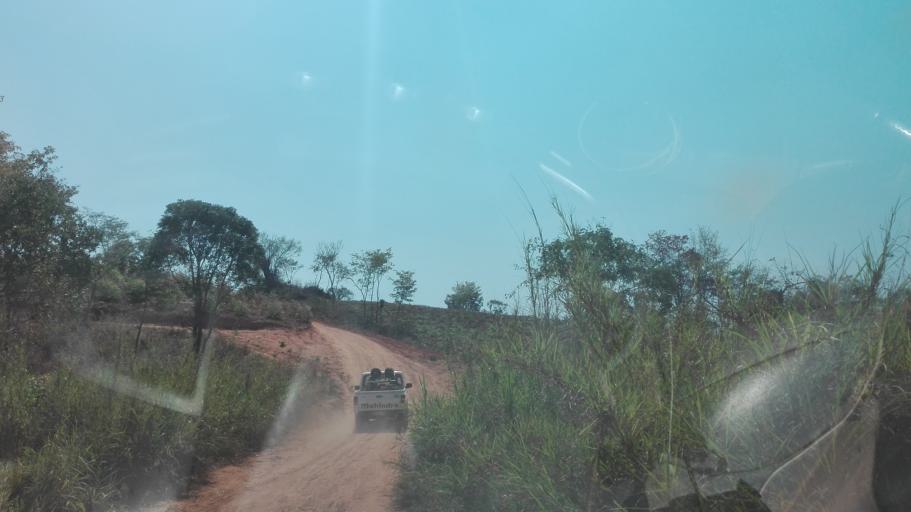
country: MZ
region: Nampula
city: Mutuali
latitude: -15.7092
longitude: 37.1759
